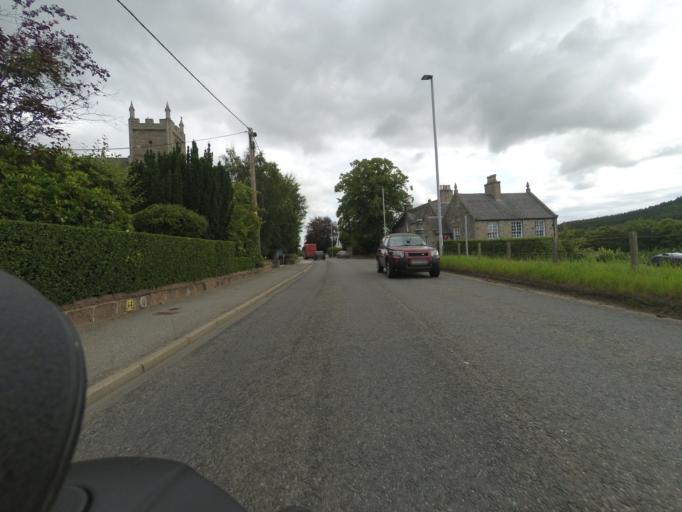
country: GB
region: Scotland
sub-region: Aberdeenshire
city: Banchory
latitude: 57.0523
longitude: -2.4849
